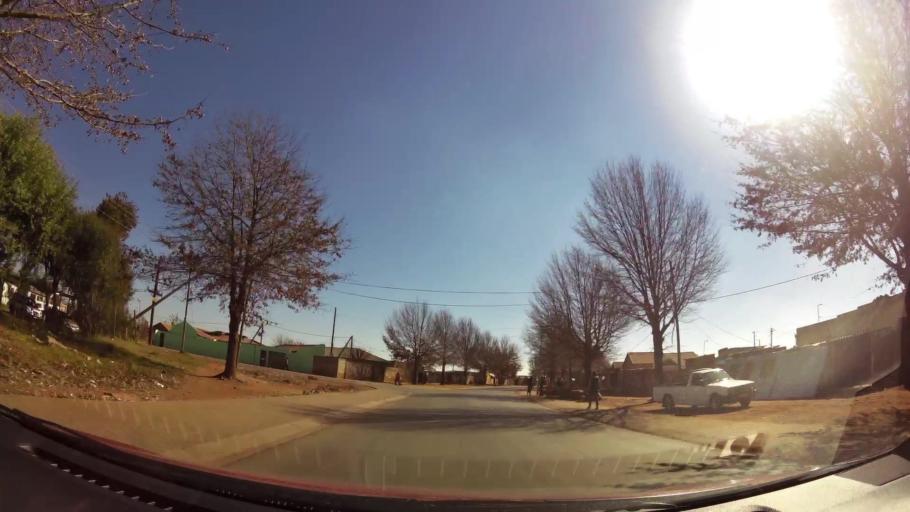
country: ZA
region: Gauteng
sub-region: City of Johannesburg Metropolitan Municipality
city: Soweto
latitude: -26.2197
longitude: 27.8328
